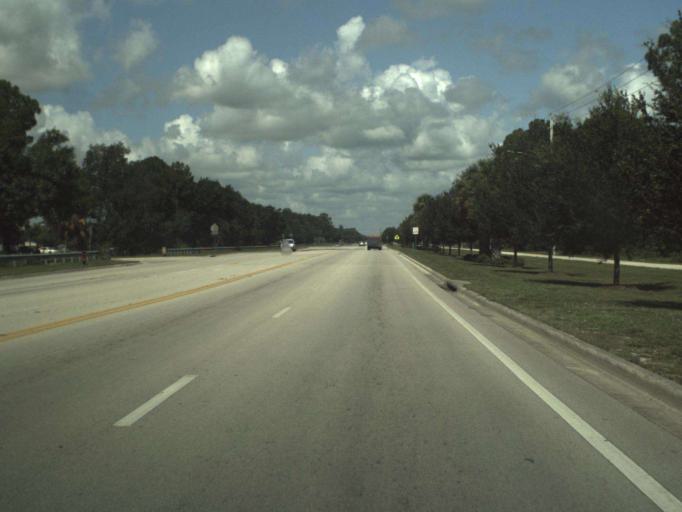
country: US
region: Florida
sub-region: Indian River County
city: Florida Ridge
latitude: 27.5872
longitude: -80.4064
